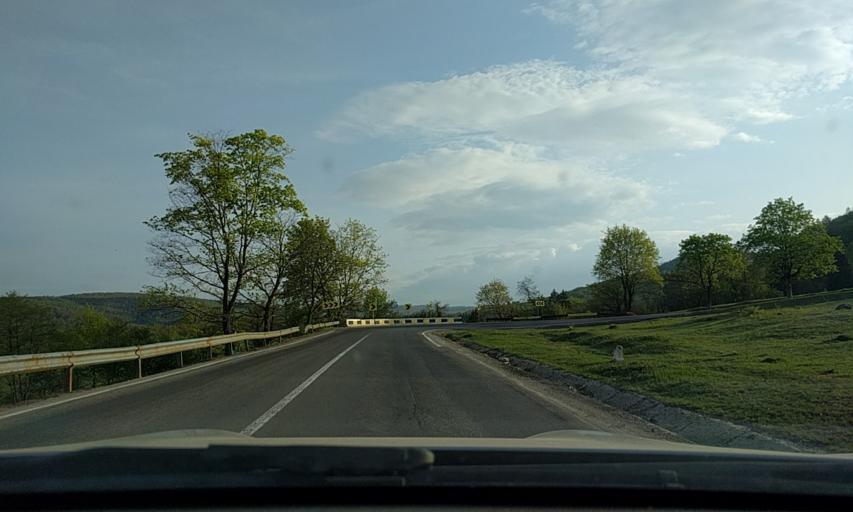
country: RO
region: Covasna
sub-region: Comuna Bretcu
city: Bretcu
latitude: 46.0450
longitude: 26.3345
